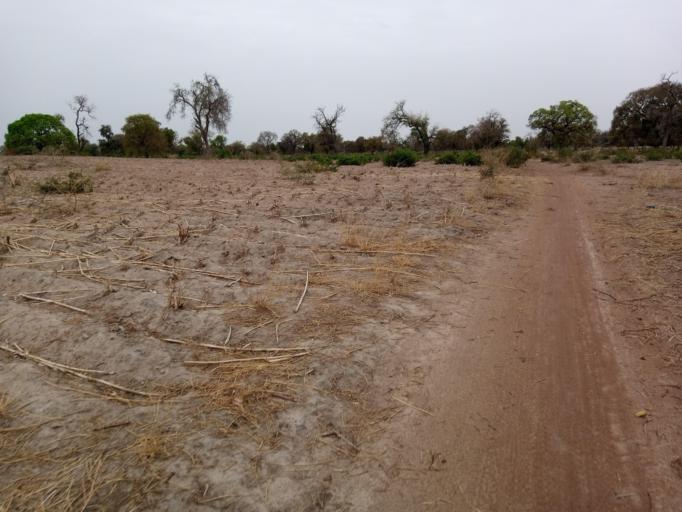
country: BF
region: Boucle du Mouhoun
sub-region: Province de la Kossi
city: Nouna
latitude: 12.7684
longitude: -4.0593
